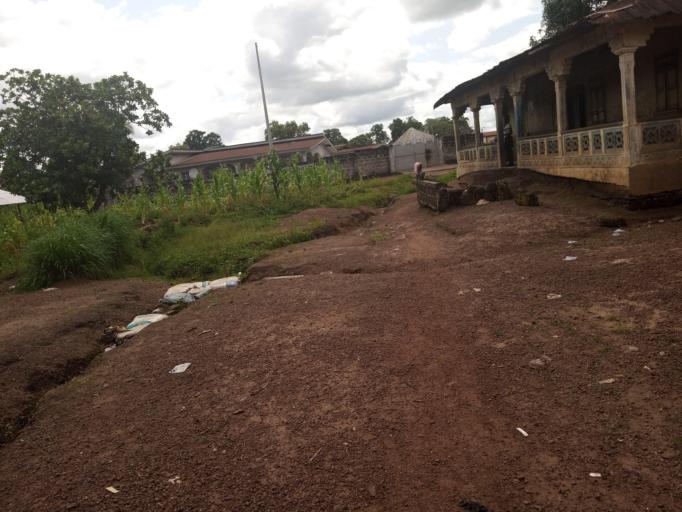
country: SL
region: Northern Province
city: Kamakwie
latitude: 9.4943
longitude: -12.2428
